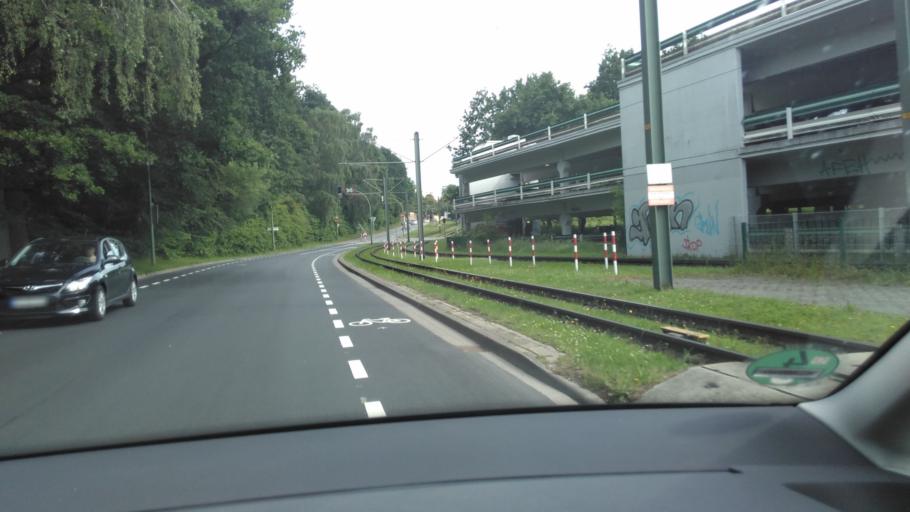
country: DE
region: North Rhine-Westphalia
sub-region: Regierungsbezirk Detmold
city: Bielefeld
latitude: 52.0389
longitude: 8.4978
